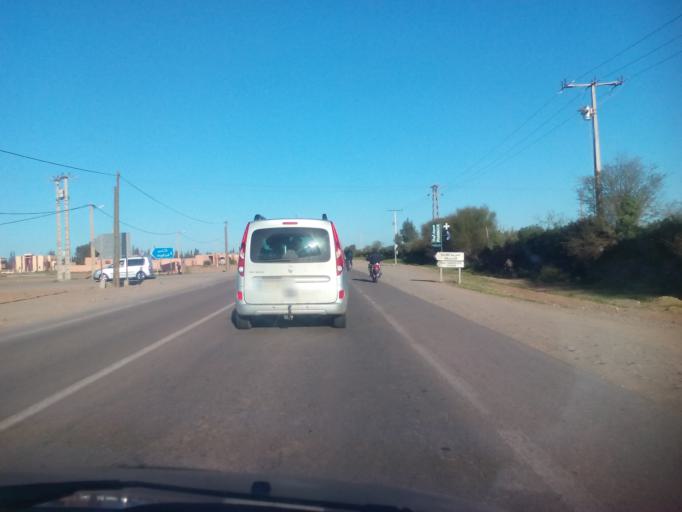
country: MA
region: Marrakech-Tensift-Al Haouz
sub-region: Marrakech
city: Marrakesh
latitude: 31.6306
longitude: -8.1656
